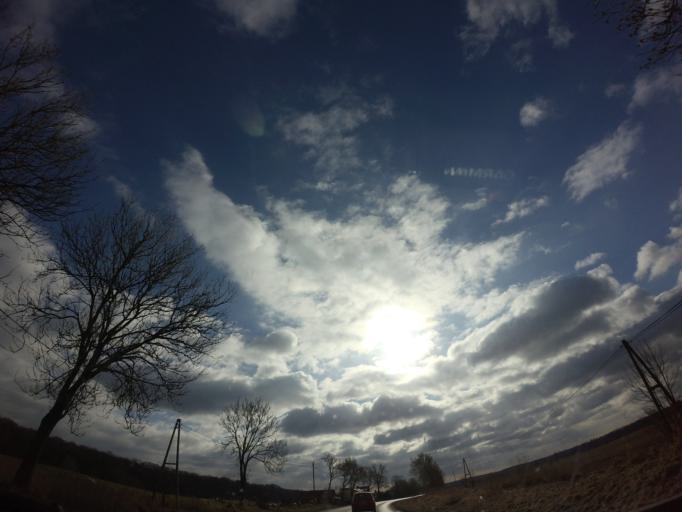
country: PL
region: West Pomeranian Voivodeship
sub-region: Powiat mysliborski
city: Barlinek
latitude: 52.9667
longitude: 15.1855
